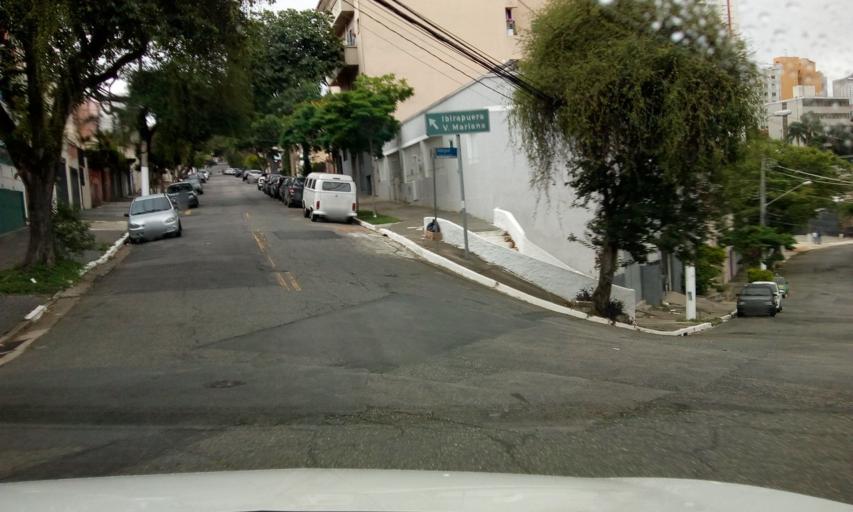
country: BR
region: Sao Paulo
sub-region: Sao Paulo
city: Sao Paulo
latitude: -23.5826
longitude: -46.6333
